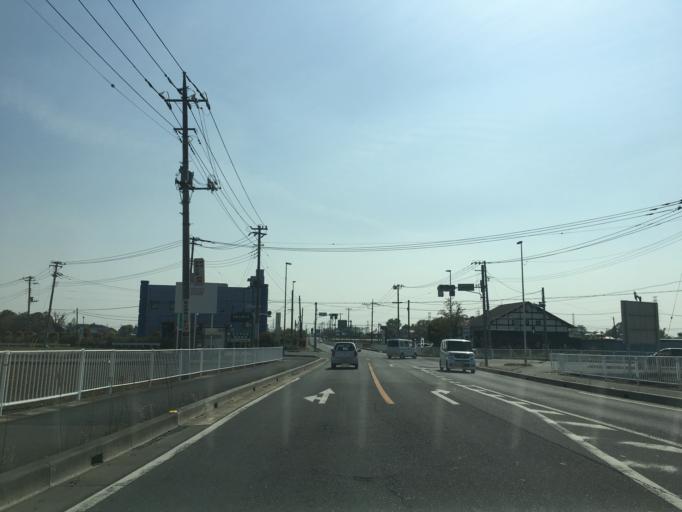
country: JP
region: Saitama
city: Sugito
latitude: 36.0160
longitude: 139.7274
